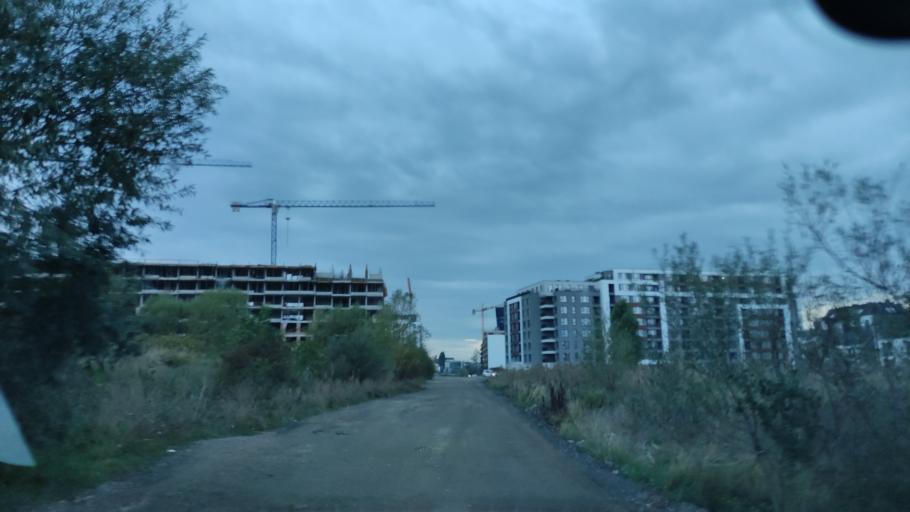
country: BG
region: Sofia-Capital
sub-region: Stolichna Obshtina
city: Sofia
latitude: 42.6538
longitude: 23.2927
